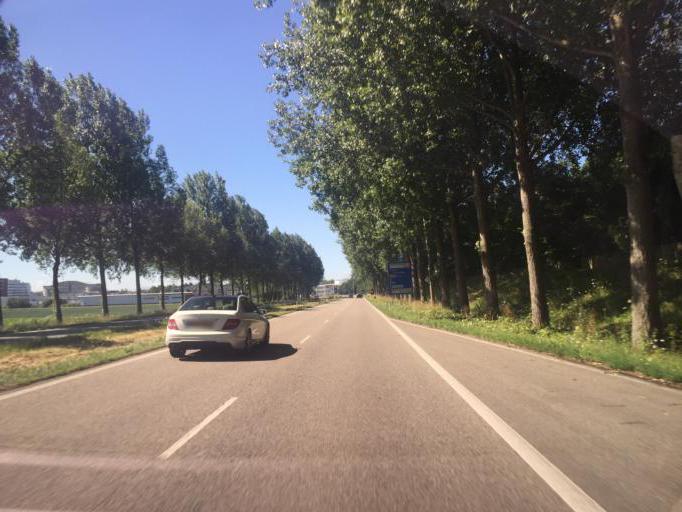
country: NL
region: North Holland
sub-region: Gemeente Haarlemmermeer
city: Hoofddorp
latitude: 52.3014
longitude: 4.7120
